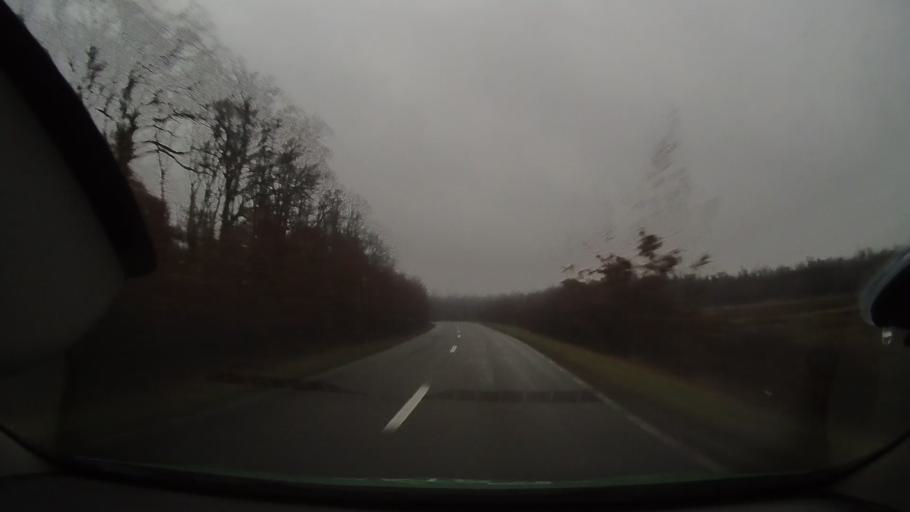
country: RO
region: Arad
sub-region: Comuna Beliu
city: Beliu
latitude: 46.5166
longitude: 21.9565
